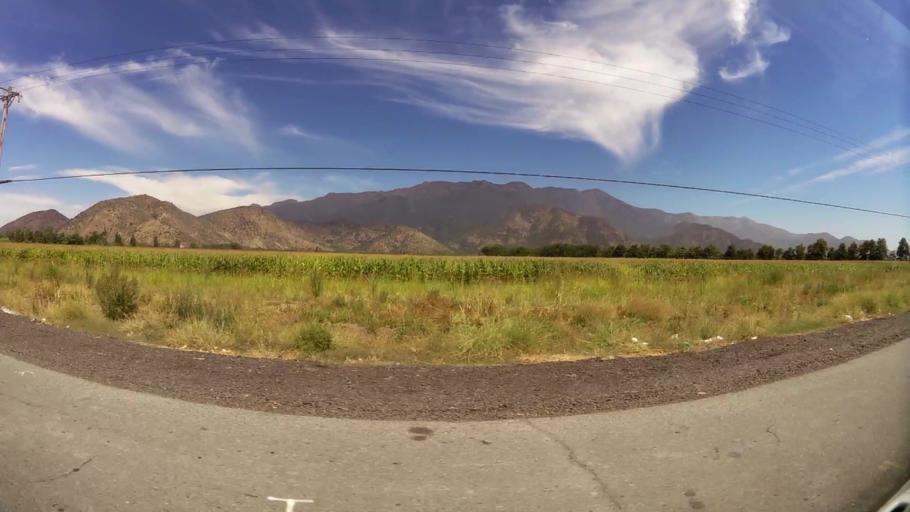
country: CL
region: O'Higgins
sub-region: Provincia de Cachapoal
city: Graneros
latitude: -34.0173
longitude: -70.7037
